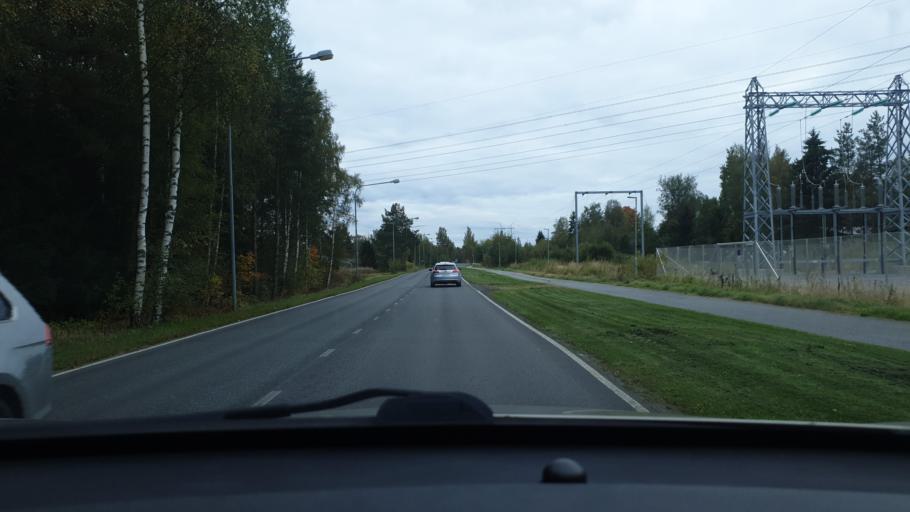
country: FI
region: Ostrobothnia
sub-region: Vaasa
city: Teeriniemi
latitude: 63.0932
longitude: 21.6979
